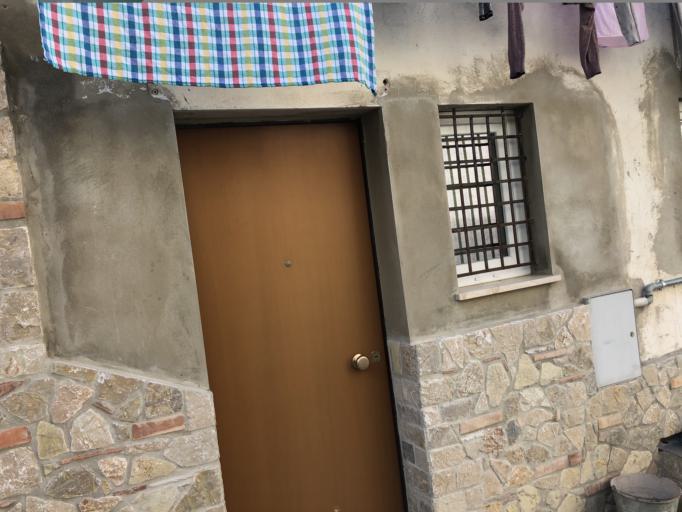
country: IT
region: Basilicate
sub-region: Provincia di Potenza
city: Pignola
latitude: 40.5760
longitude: 15.7878
